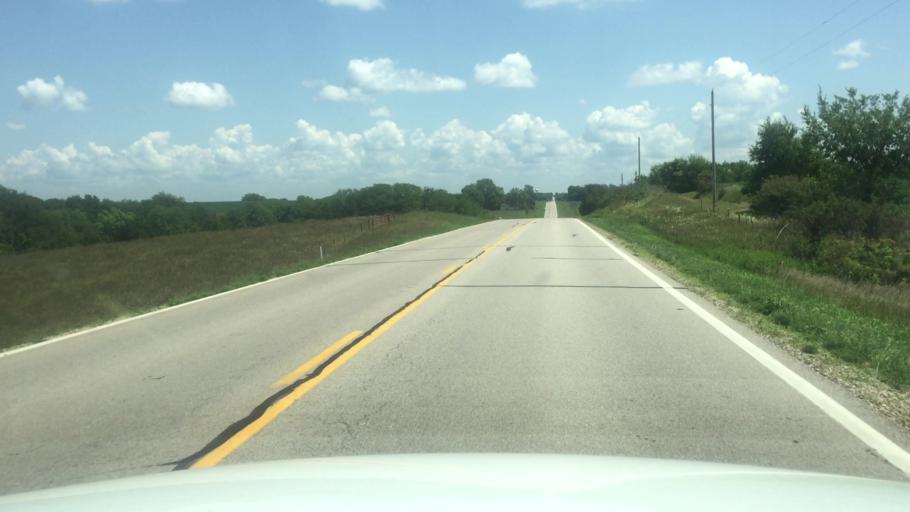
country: US
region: Kansas
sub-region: Brown County
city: Horton
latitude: 39.6674
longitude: -95.5764
